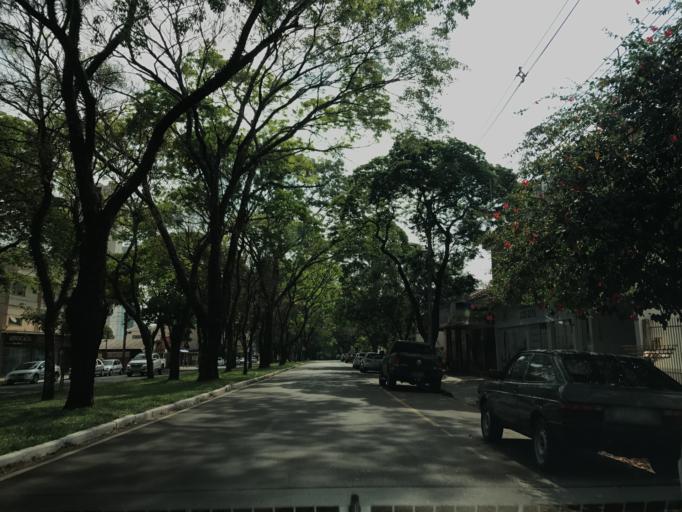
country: BR
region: Parana
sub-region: Maringa
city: Maringa
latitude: -23.4268
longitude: -51.9237
